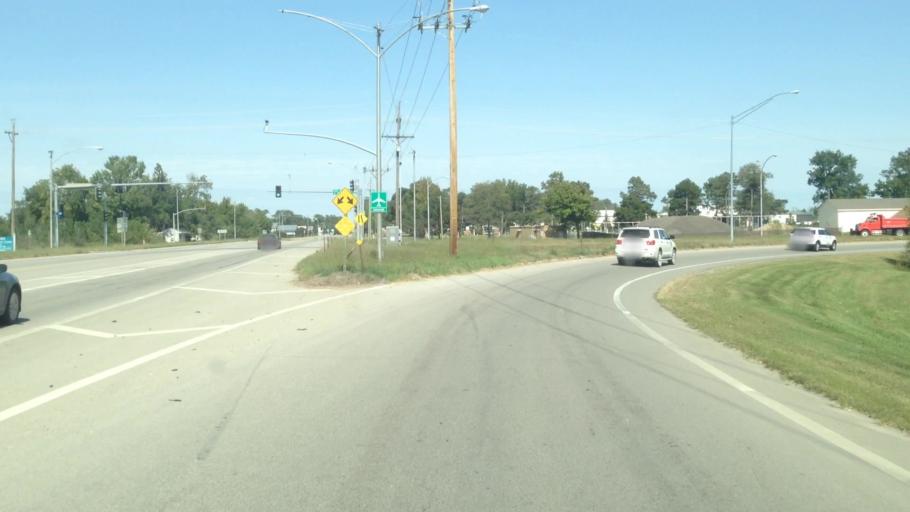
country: US
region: Kansas
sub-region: Douglas County
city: Lawrence
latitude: 38.9997
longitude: -95.2333
